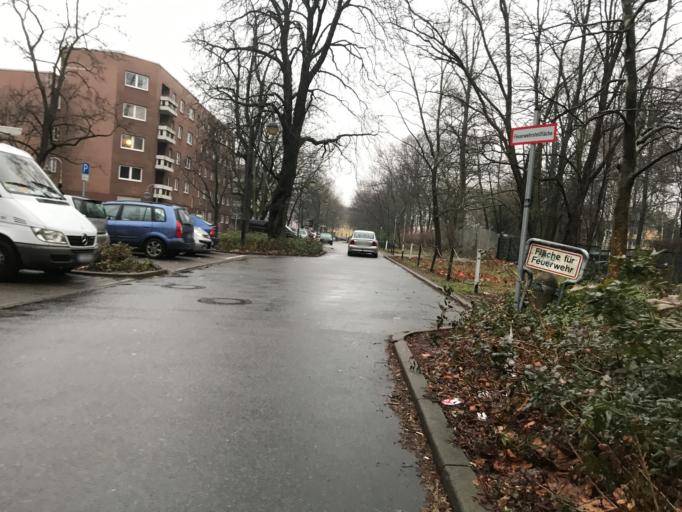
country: DE
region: Berlin
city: Tiergarten Bezirk
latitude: 52.5248
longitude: 13.3626
